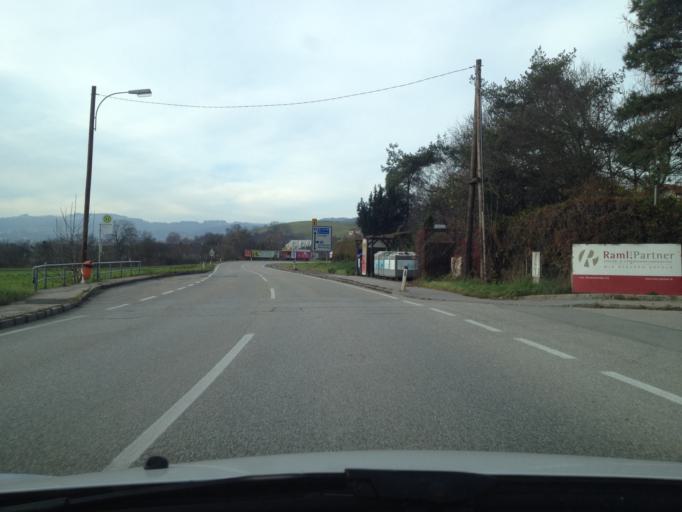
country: AT
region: Upper Austria
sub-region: Politischer Bezirk Urfahr-Umgebung
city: Altenberg bei Linz
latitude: 48.3264
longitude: 14.3379
